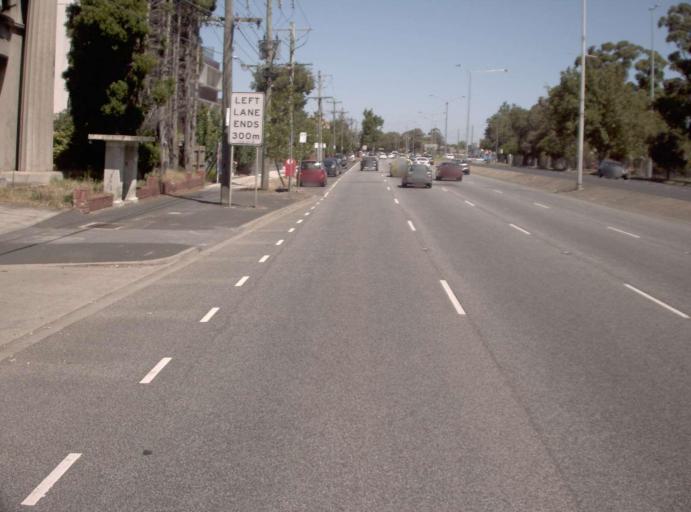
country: AU
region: Victoria
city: Glen Huntly
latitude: -37.8783
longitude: 145.0478
